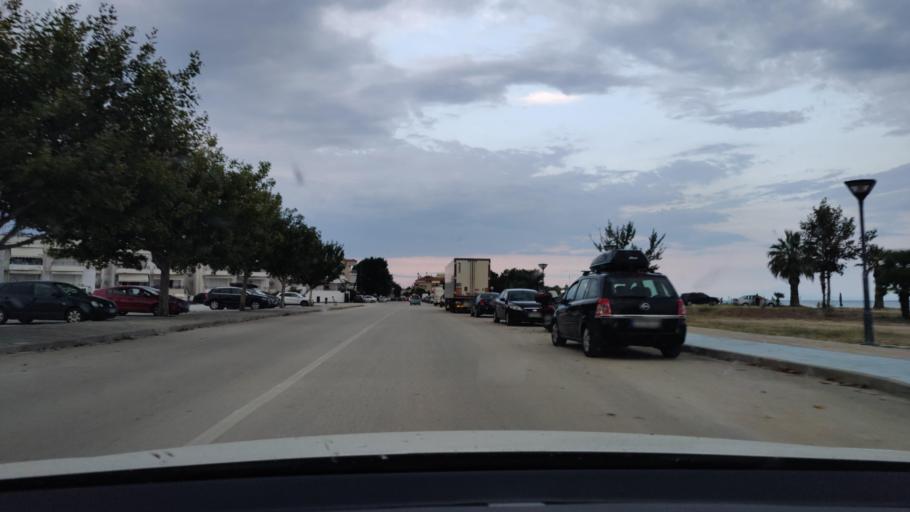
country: GR
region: East Macedonia and Thrace
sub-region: Nomos Kavalas
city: Paralia Ofryniou
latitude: 40.7666
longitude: 23.8976
